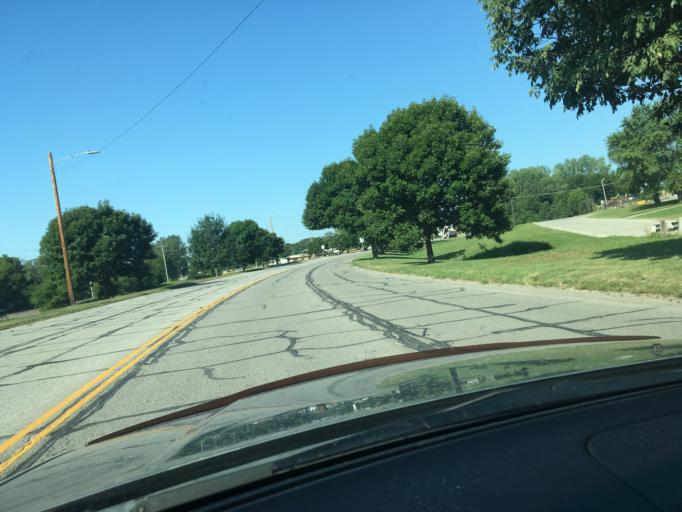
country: US
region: Kansas
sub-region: Atchison County
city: Atchison
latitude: 39.5564
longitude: -95.1504
